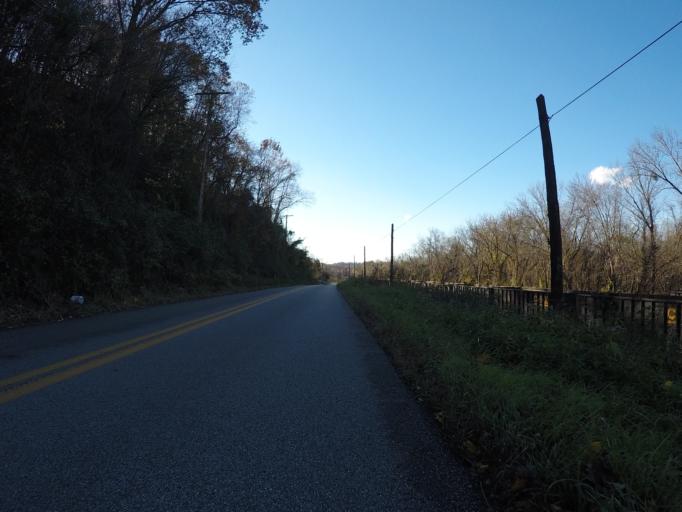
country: US
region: West Virginia
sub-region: Wayne County
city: Ceredo
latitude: 38.3928
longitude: -82.5516
